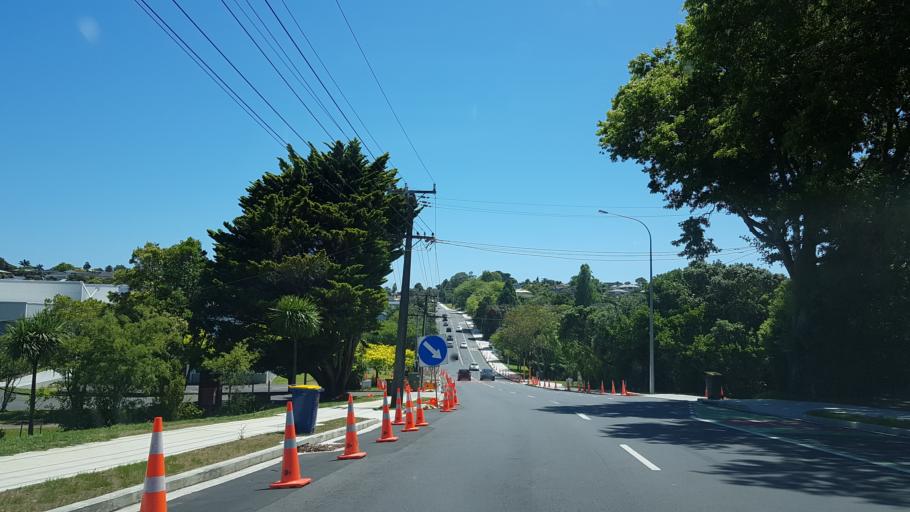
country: NZ
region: Auckland
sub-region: Auckland
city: North Shore
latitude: -36.8084
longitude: 174.7436
